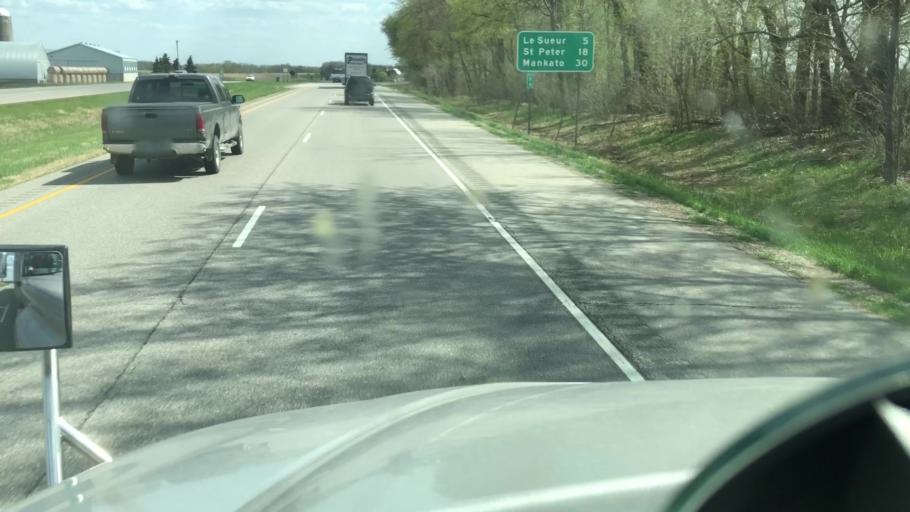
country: US
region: Minnesota
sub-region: Le Sueur County
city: Le Sueur
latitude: 44.5391
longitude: -93.8489
